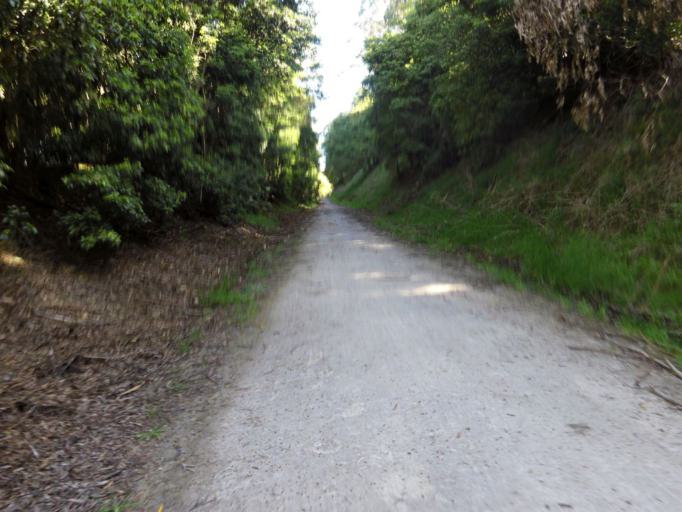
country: AU
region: Victoria
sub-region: Latrobe
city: Morwell
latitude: -38.6806
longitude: 146.1578
